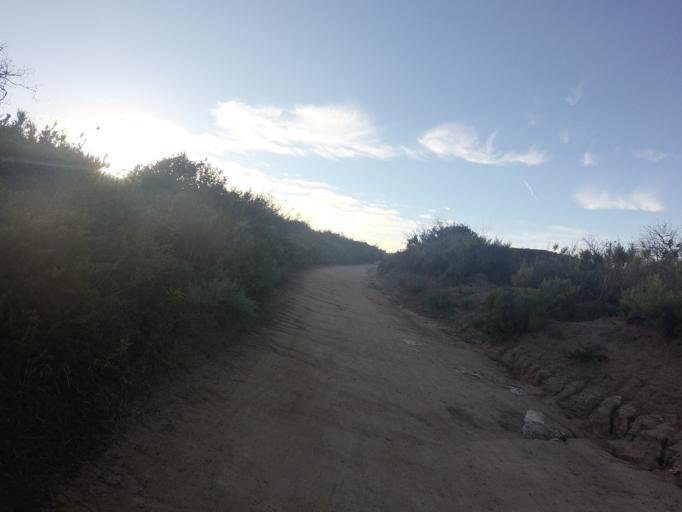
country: US
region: California
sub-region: Orange County
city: Laguna Beach
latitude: 33.5916
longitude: -117.7782
